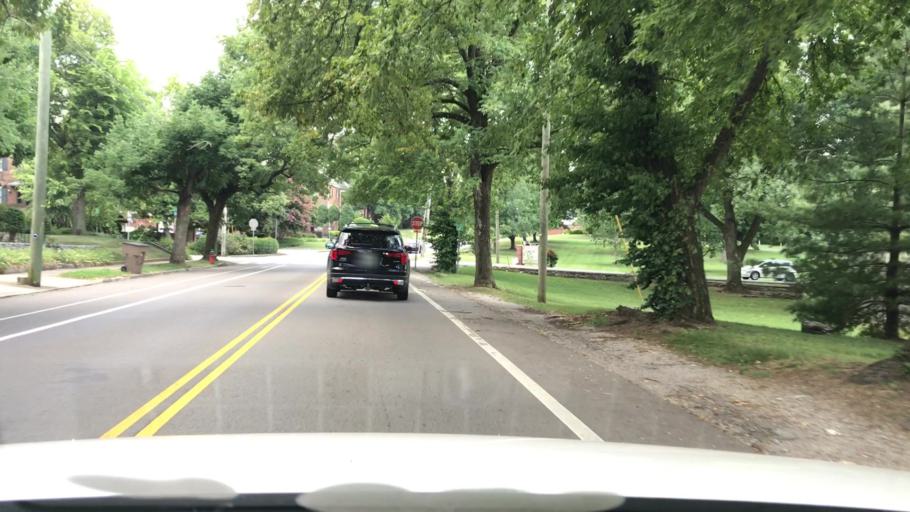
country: US
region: Tennessee
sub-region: Davidson County
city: Nashville
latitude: 36.1332
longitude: -86.8226
